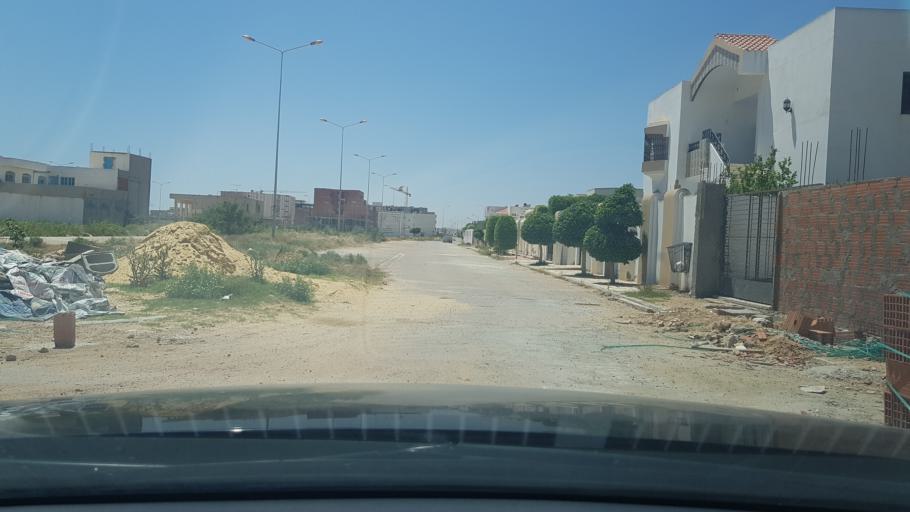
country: TN
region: Safaqis
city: Al Qarmadah
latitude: 34.8369
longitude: 10.7637
